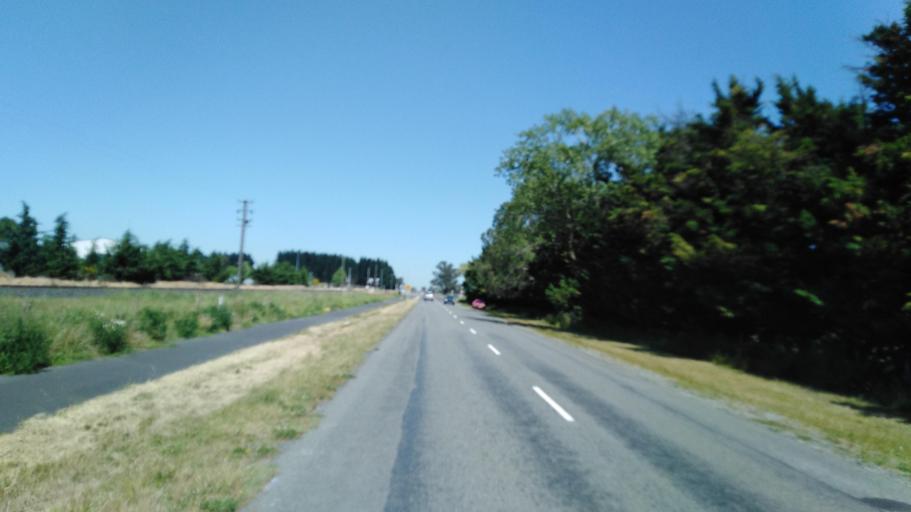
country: NZ
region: Canterbury
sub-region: Selwyn District
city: Prebbleton
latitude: -43.5594
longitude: 172.4601
